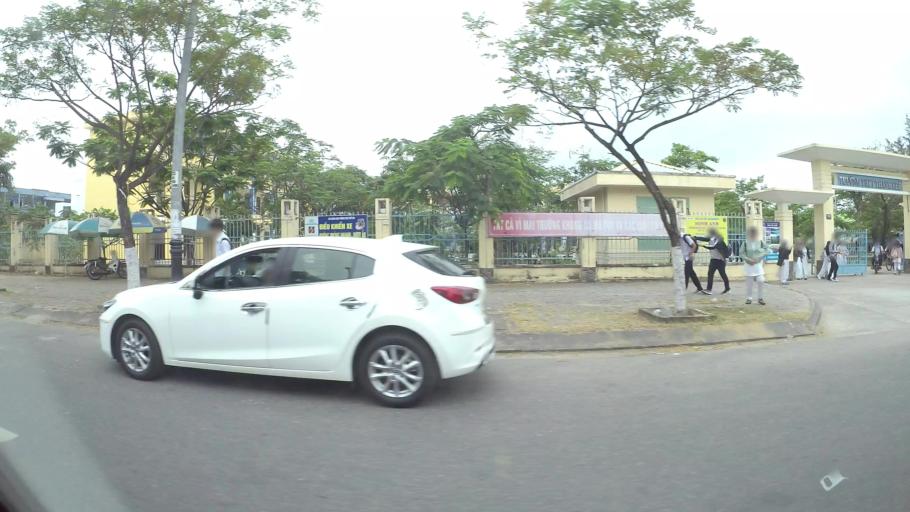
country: VN
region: Da Nang
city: Lien Chieu
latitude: 16.0764
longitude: 108.1671
